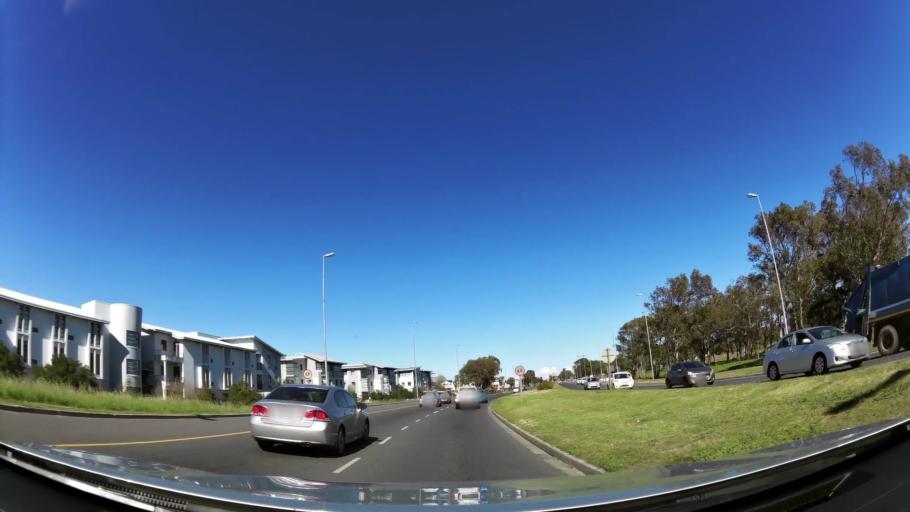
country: ZA
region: Western Cape
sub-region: Cape Winelands District Municipality
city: Stellenbosch
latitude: -34.0858
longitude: 18.8201
